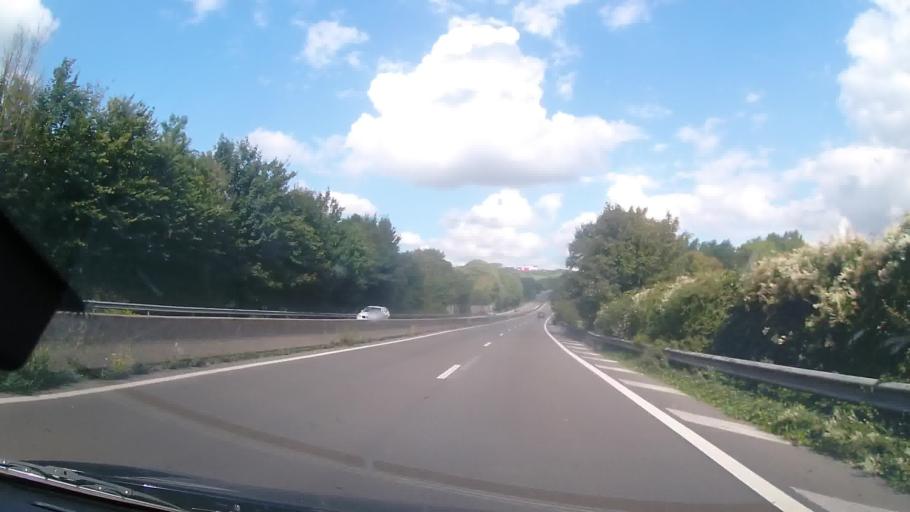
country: FR
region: Nord-Pas-de-Calais
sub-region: Departement du Pas-de-Calais
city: Wimille
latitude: 50.7605
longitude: 1.6340
